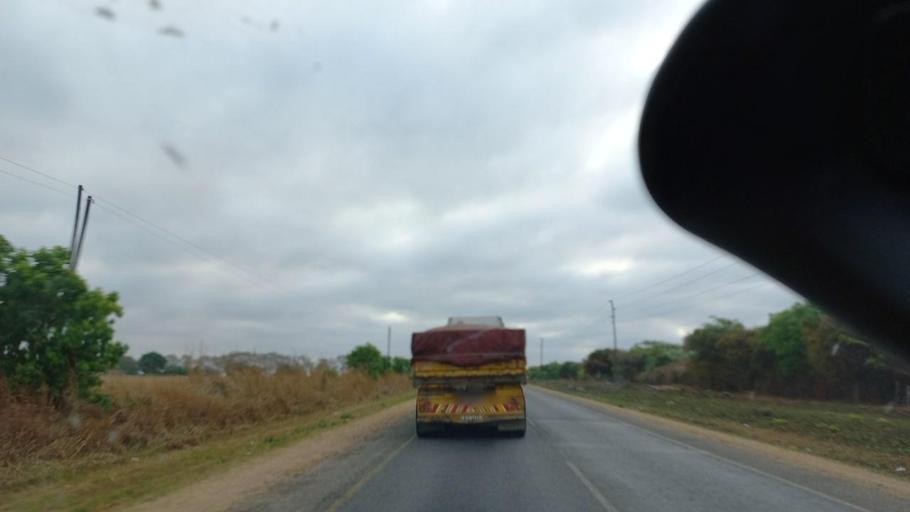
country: ZM
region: Lusaka
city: Chongwe
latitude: -15.3499
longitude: 28.5647
